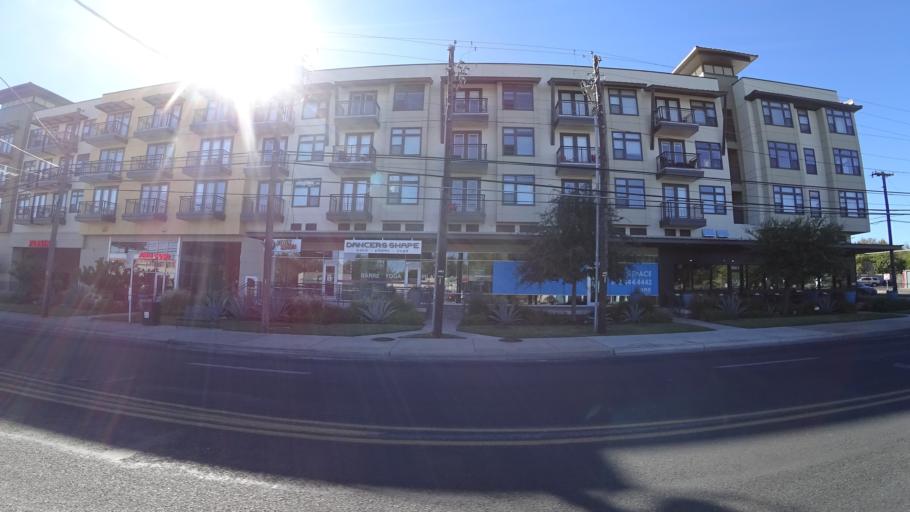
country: US
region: Texas
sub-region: Travis County
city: Austin
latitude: 30.3277
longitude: -97.7397
